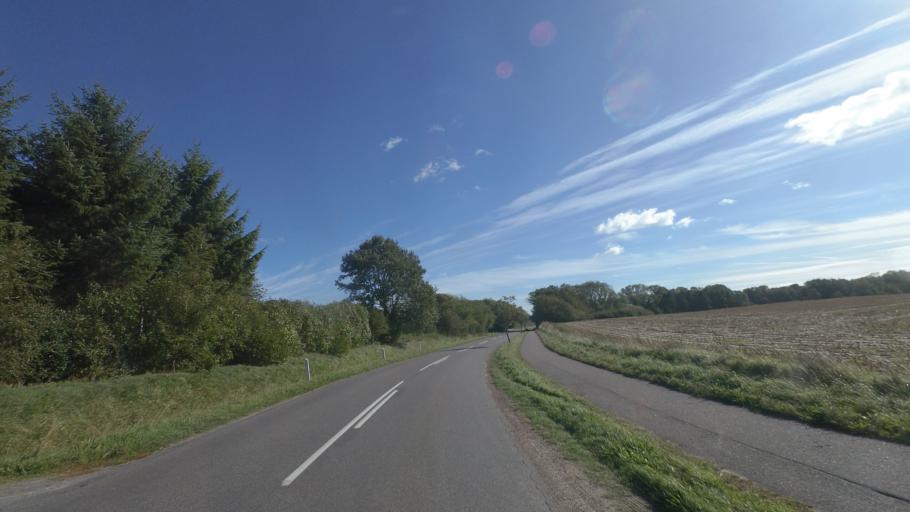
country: DK
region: Capital Region
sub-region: Bornholm Kommune
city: Akirkeby
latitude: 55.0091
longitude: 14.9930
